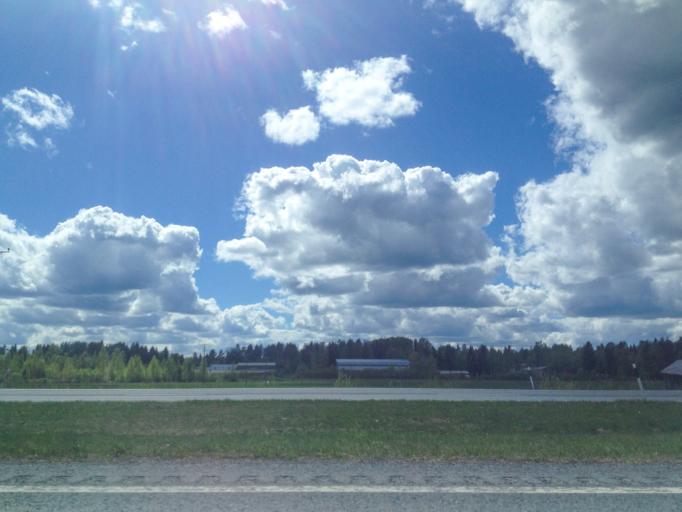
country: FI
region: Haeme
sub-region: Haemeenlinna
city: Kalvola
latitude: 61.1003
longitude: 24.1612
